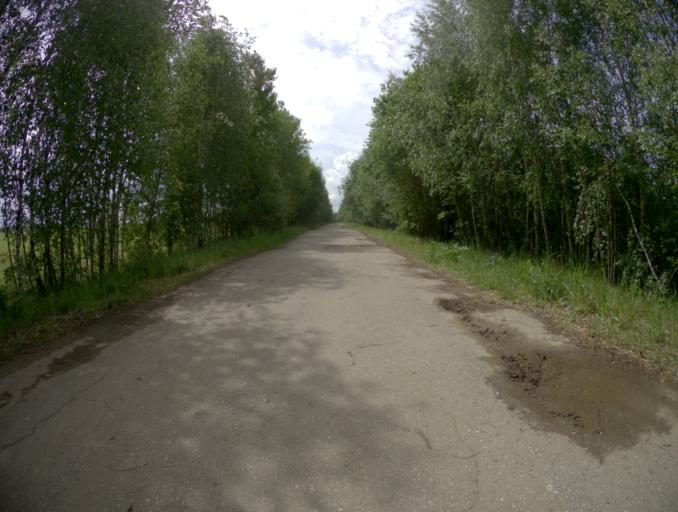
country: RU
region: Vladimir
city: Stavrovo
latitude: 56.1133
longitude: 39.9715
